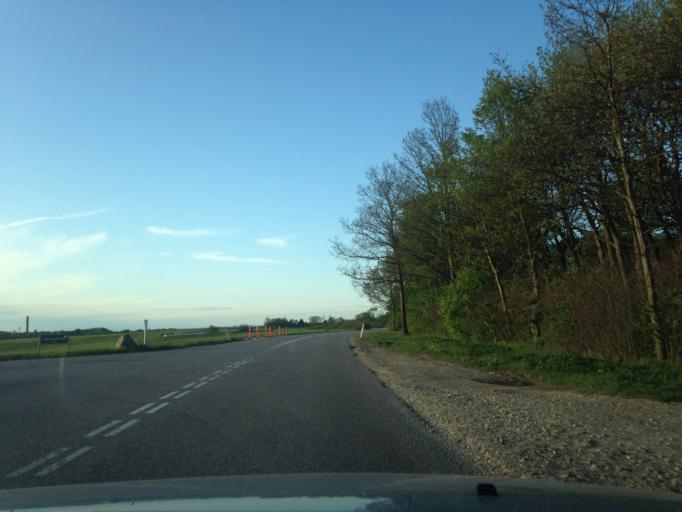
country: DK
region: Zealand
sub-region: Greve Kommune
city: Tune
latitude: 55.6222
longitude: 12.1847
